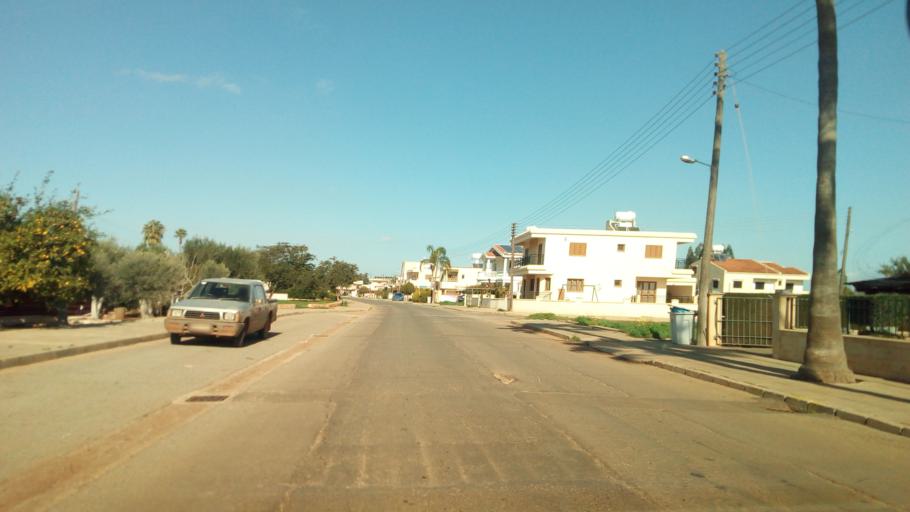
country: CY
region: Ammochostos
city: Avgorou
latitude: 35.0260
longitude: 33.8397
